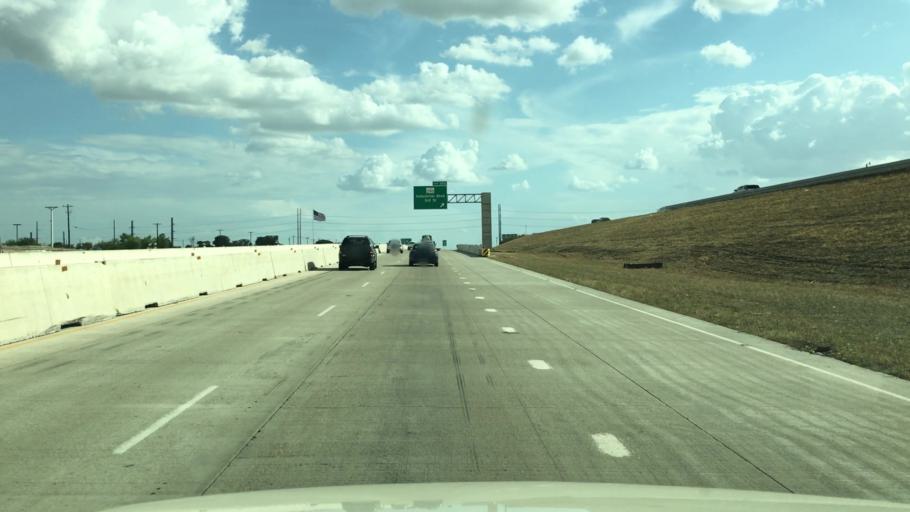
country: US
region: Texas
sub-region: Bell County
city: Temple
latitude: 31.1375
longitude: -97.3307
